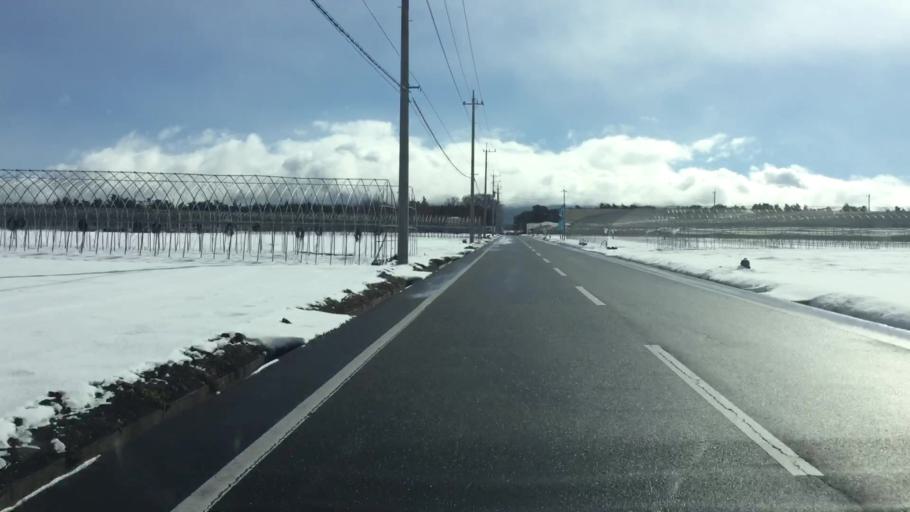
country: JP
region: Gunma
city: Numata
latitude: 36.6303
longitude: 139.0899
